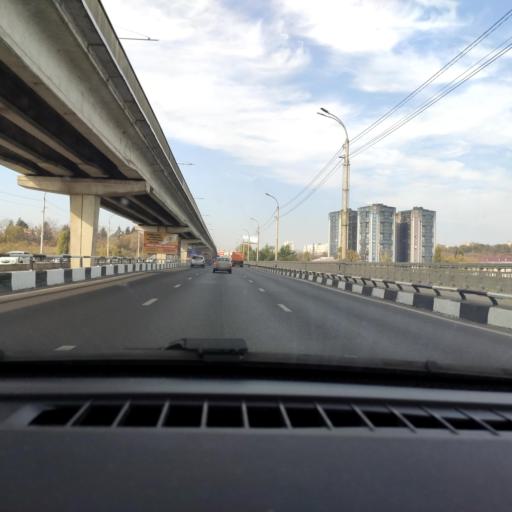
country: RU
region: Voronezj
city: Voronezh
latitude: 51.6927
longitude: 39.2372
